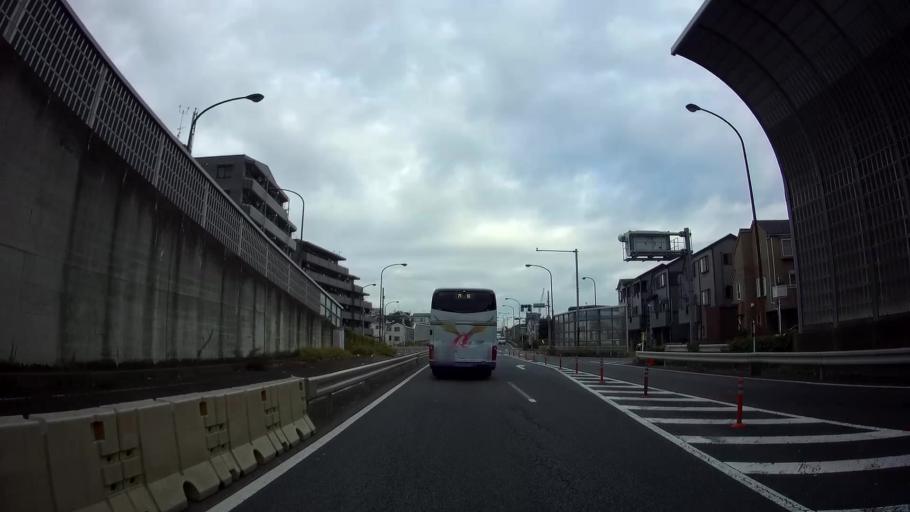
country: JP
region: Saitama
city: Wako
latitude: 35.7725
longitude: 139.6511
